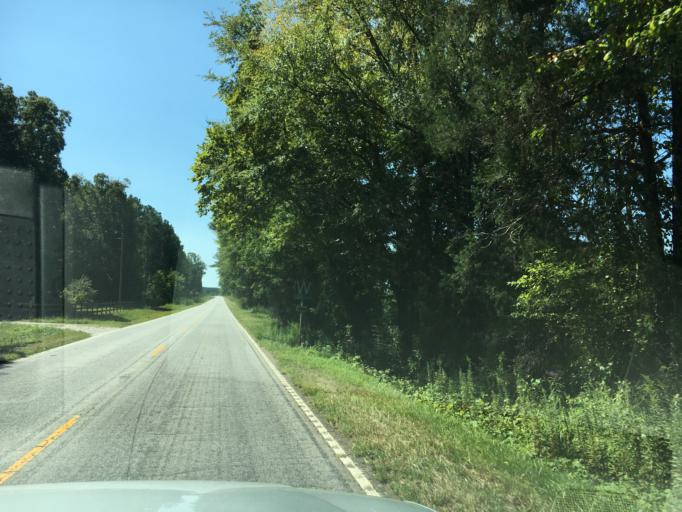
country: US
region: South Carolina
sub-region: Laurens County
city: Joanna
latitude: 34.3691
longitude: -81.8604
